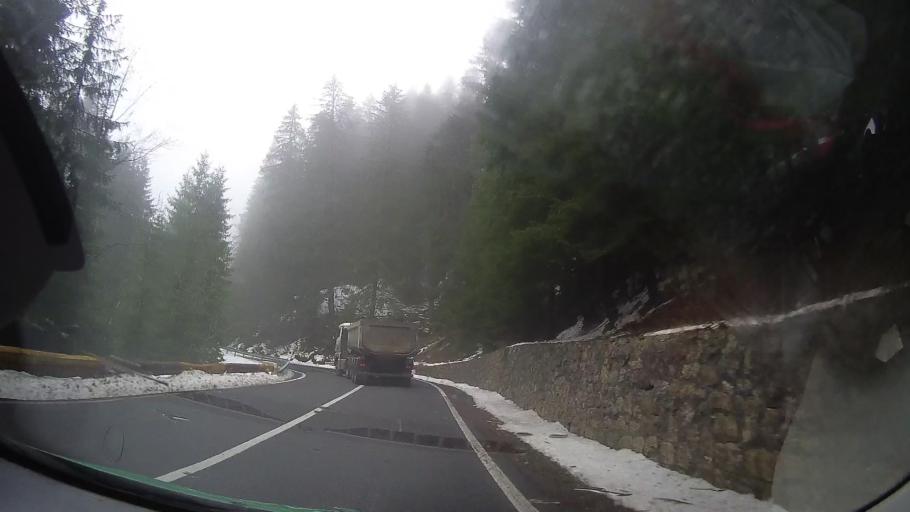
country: RO
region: Harghita
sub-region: Municipiul Gheorgheni
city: Gheorgheni
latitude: 46.7759
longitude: 25.7331
